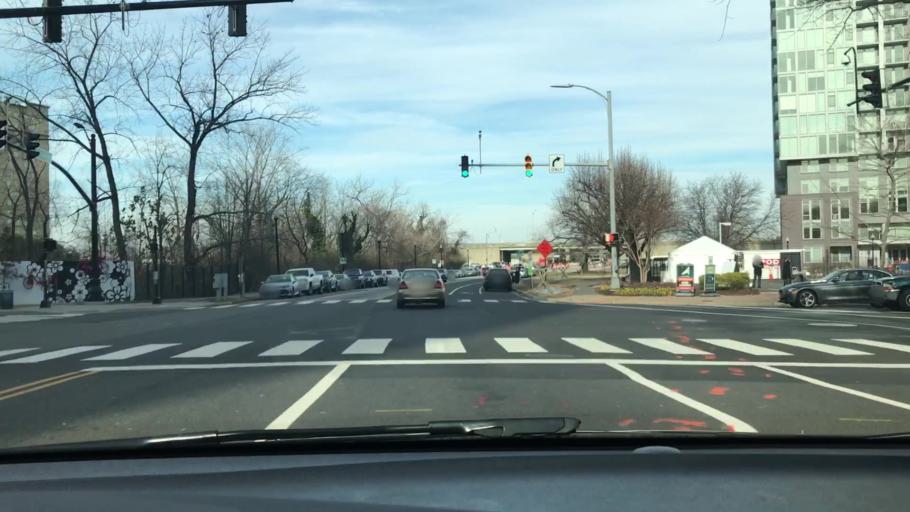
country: US
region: Washington, D.C.
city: Washington, D.C.
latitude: 38.8628
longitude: -77.0542
